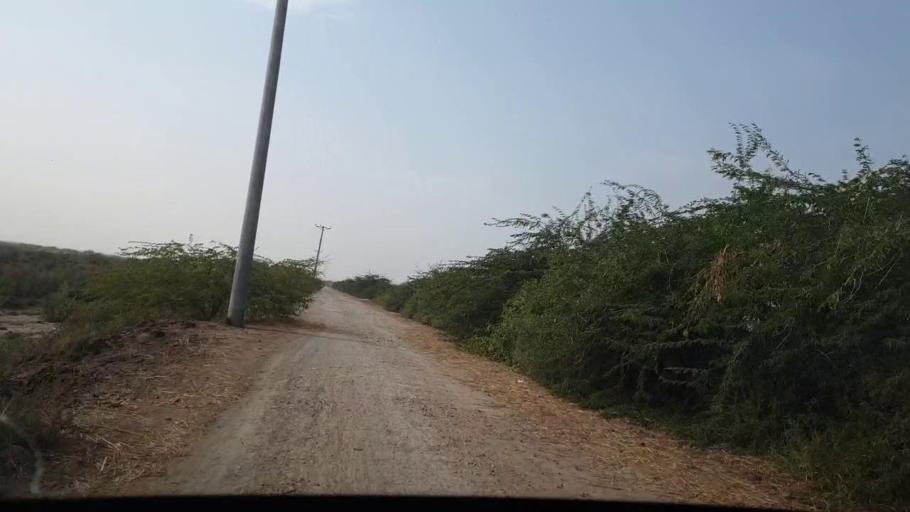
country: PK
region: Sindh
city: Chuhar Jamali
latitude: 24.2711
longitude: 67.8964
